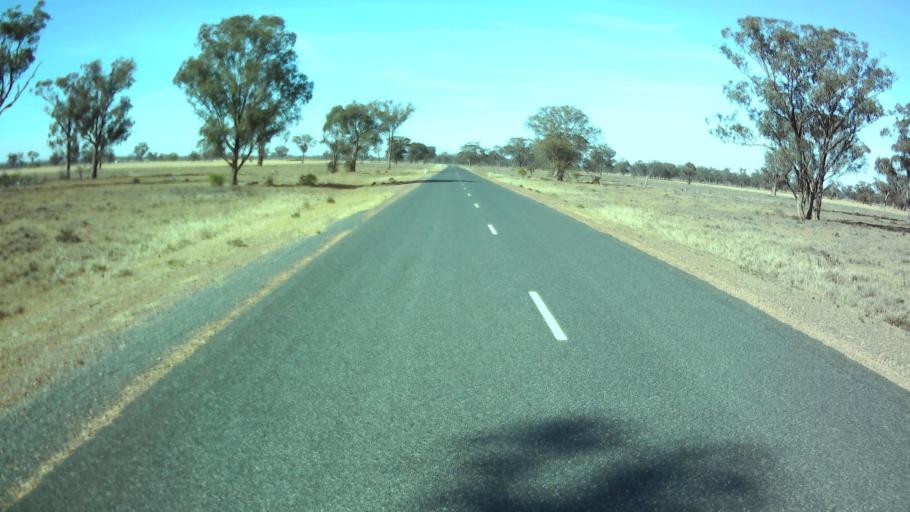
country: AU
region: New South Wales
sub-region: Weddin
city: Grenfell
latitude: -34.0746
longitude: 147.9009
